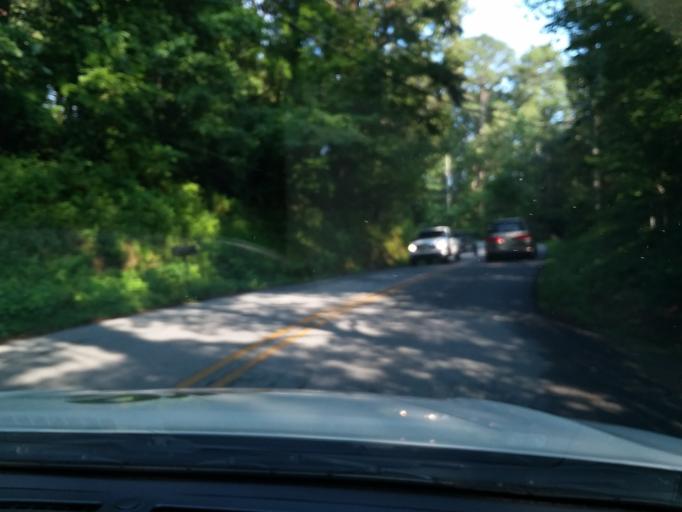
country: US
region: Georgia
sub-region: Rabun County
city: Clayton
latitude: 34.7751
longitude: -83.4277
